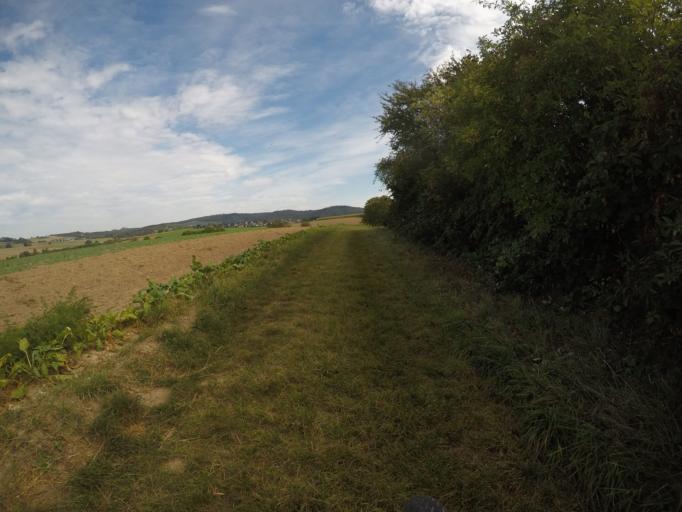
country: DE
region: Baden-Wuerttemberg
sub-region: Karlsruhe Region
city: Kurnbach
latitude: 49.0702
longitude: 8.8259
